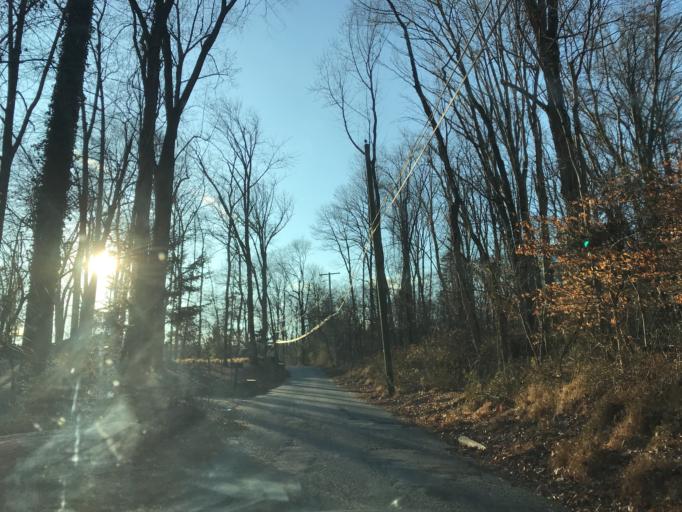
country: US
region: Maryland
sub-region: Baltimore County
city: Lutherville
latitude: 39.3799
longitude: -76.6480
